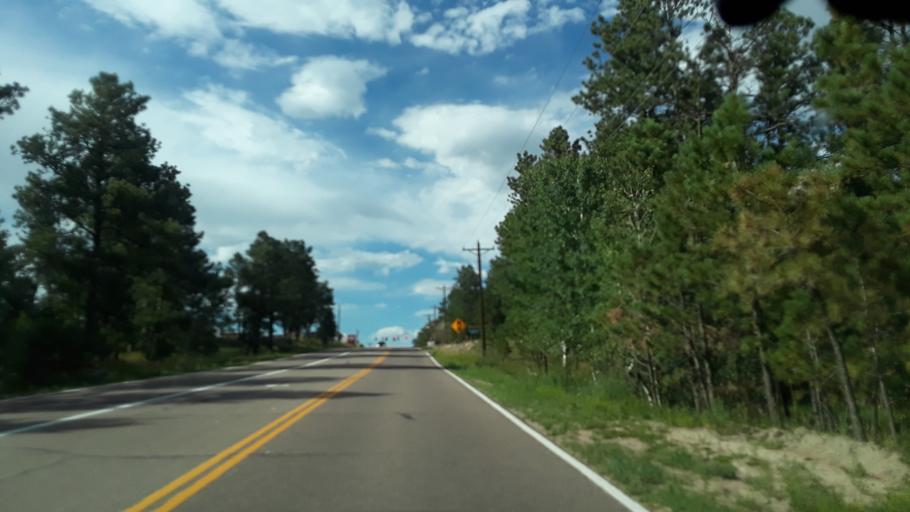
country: US
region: Colorado
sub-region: El Paso County
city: Black Forest
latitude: 39.0108
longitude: -104.7005
